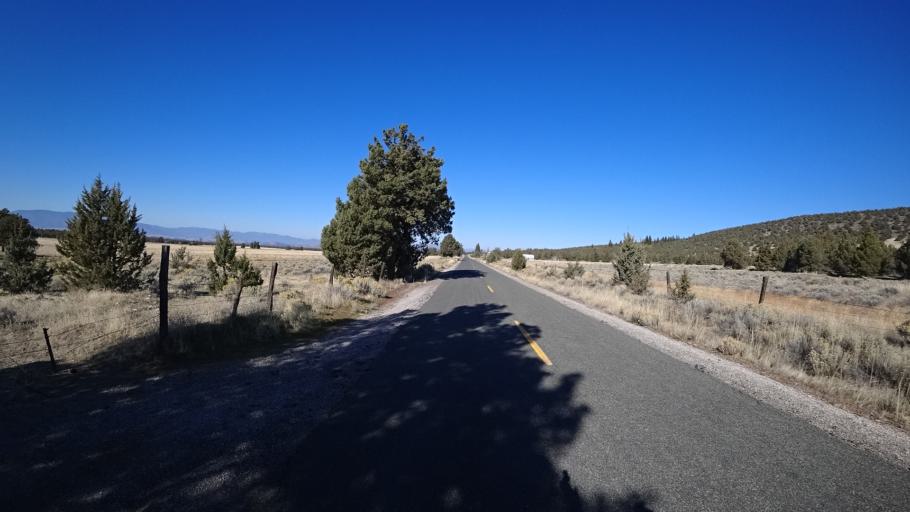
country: US
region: California
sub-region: Siskiyou County
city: Weed
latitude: 41.6164
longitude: -122.3188
